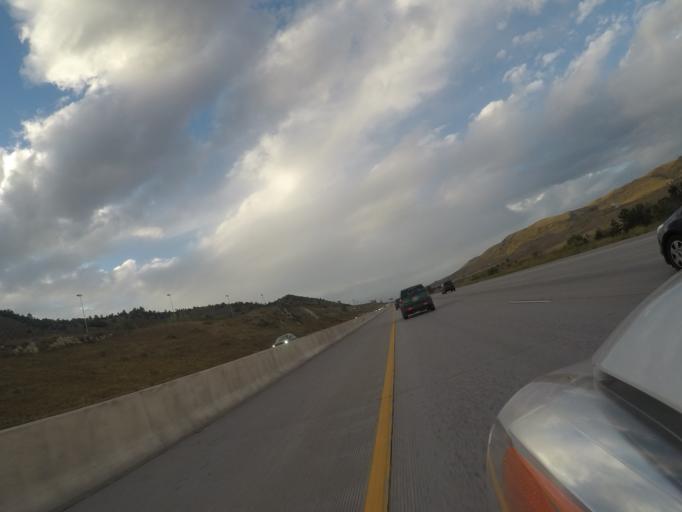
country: US
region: Colorado
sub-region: Jefferson County
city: West Pleasant View
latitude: 39.6674
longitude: -105.1868
